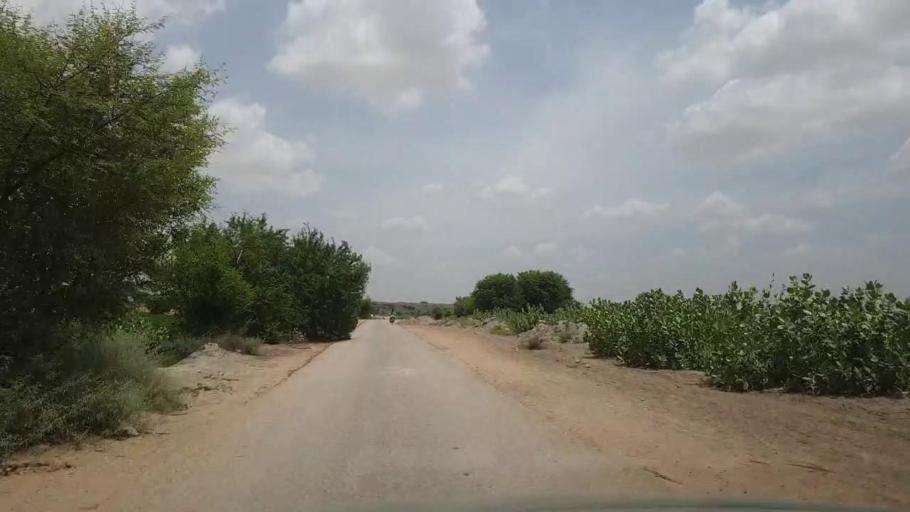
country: PK
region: Sindh
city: Kot Diji
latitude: 27.2006
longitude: 69.0607
